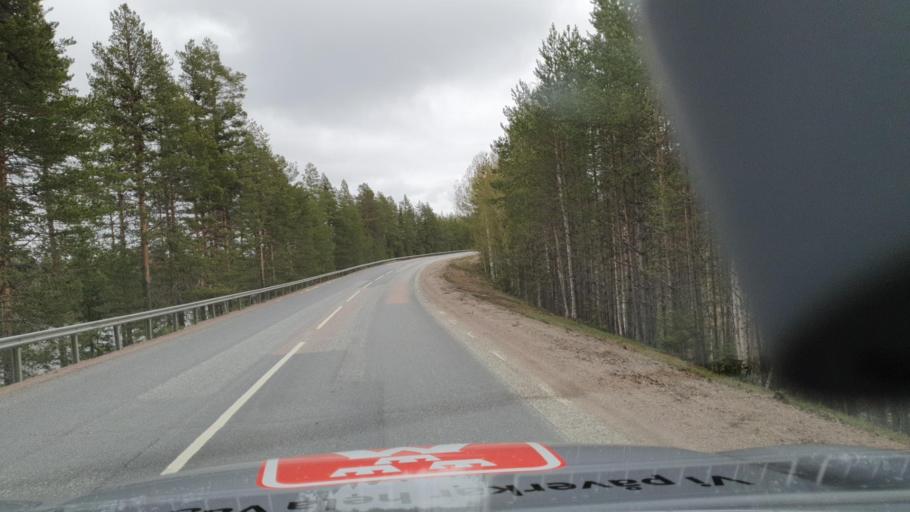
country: SE
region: Vaesternorrland
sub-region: Solleftea Kommun
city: Solleftea
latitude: 63.6465
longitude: 17.3867
